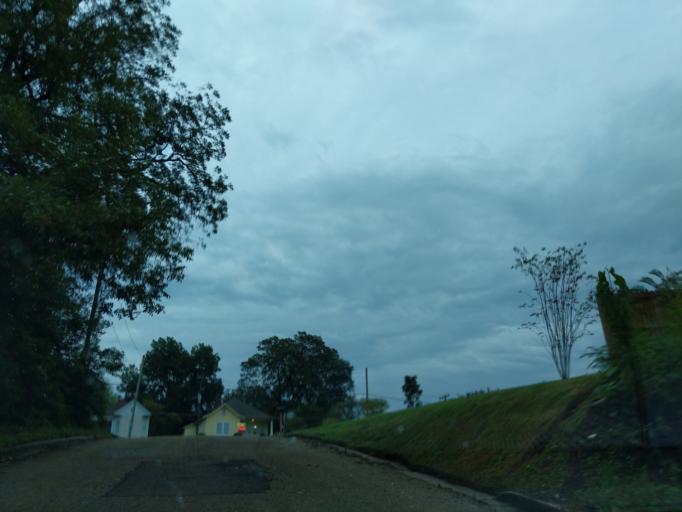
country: US
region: Mississippi
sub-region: Warren County
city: Vicksburg
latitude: 32.3338
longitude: -90.8885
